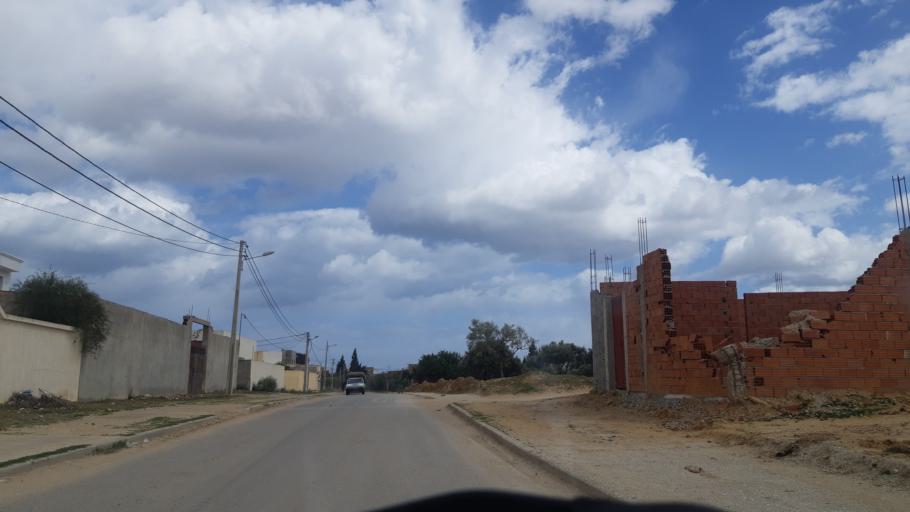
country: TN
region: Susah
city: Akouda
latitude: 35.8623
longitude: 10.5286
